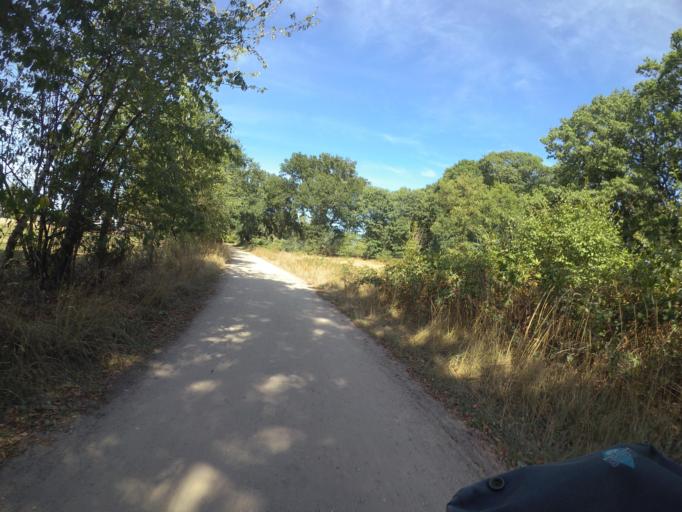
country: NL
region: Overijssel
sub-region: Gemeente Raalte
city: Raalte
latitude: 52.3520
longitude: 6.3834
